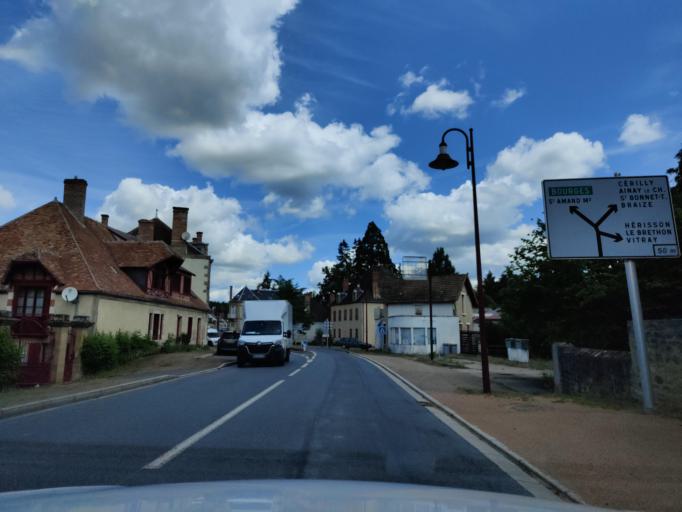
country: FR
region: Auvergne
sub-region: Departement de l'Allier
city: Vallon-en-Sully
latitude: 46.5980
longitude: 2.6135
